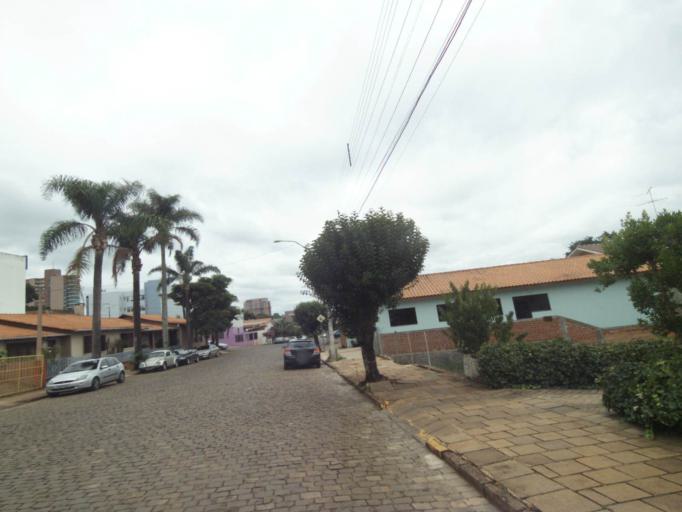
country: BR
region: Rio Grande do Sul
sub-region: Lagoa Vermelha
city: Lagoa Vermelha
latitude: -28.2085
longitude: -51.5231
